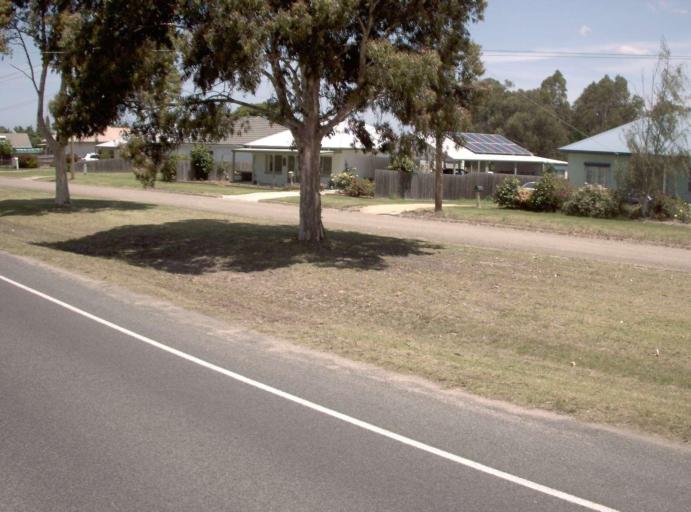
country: AU
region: Victoria
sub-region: East Gippsland
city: Bairnsdale
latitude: -37.8146
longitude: 147.6479
